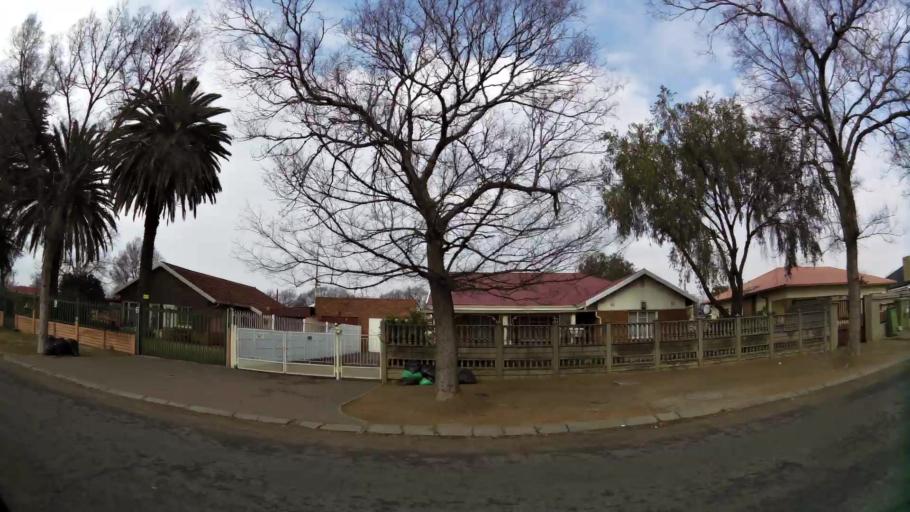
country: ZA
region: Gauteng
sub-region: Sedibeng District Municipality
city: Vanderbijlpark
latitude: -26.6925
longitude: 27.8460
